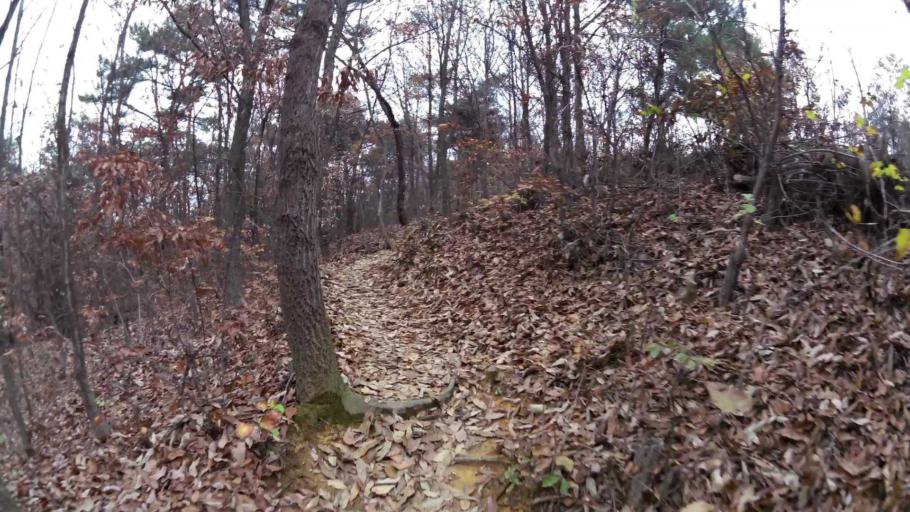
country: KR
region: Daegu
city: Daegu
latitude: 35.8614
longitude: 128.6618
